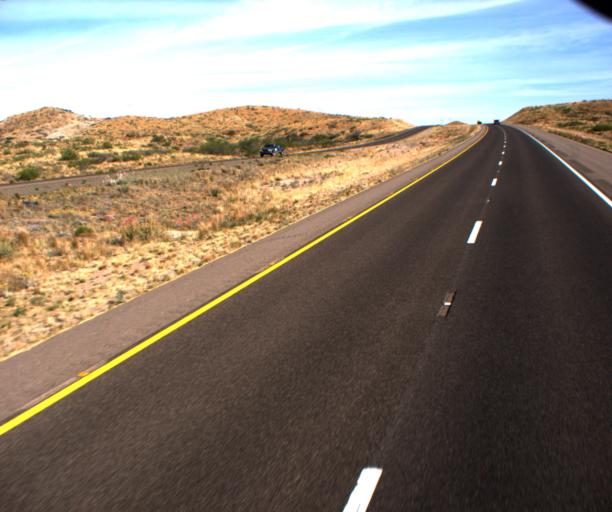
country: US
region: Arizona
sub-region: Cochise County
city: Willcox
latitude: 32.4534
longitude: -109.6642
